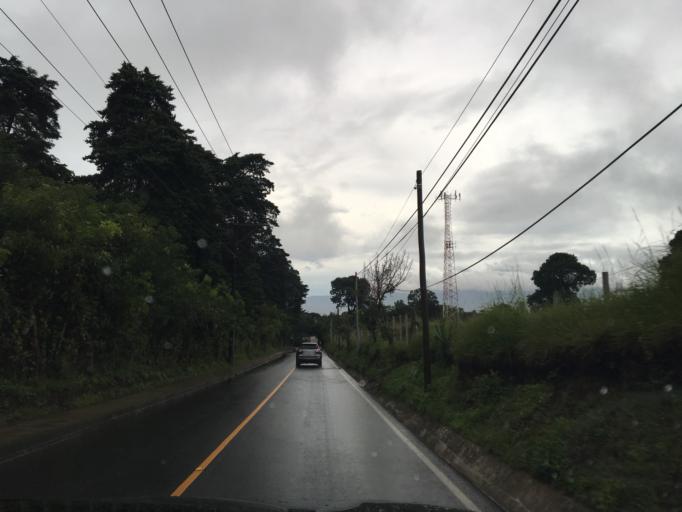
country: GT
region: Guatemala
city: Santa Catarina Pinula
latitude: 14.5581
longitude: -90.5019
